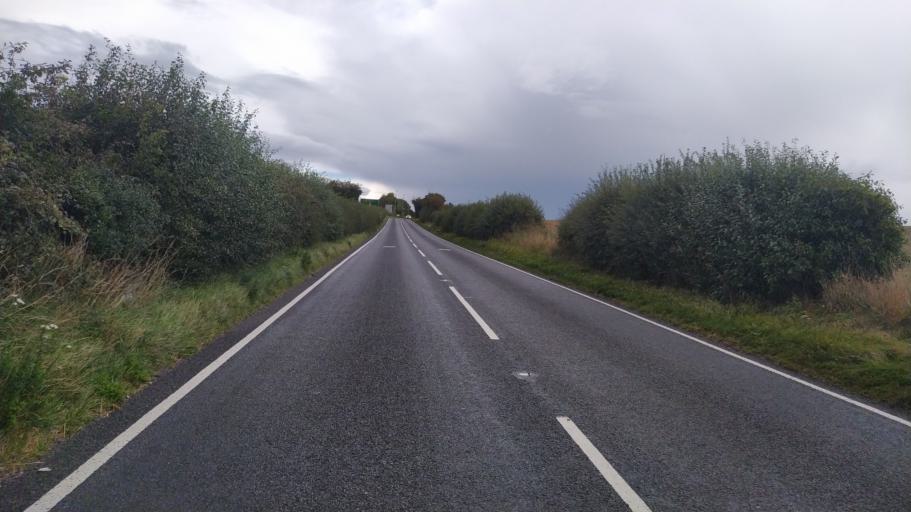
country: GB
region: England
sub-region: Wiltshire
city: Bower Chalke
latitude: 50.9461
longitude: -1.9893
